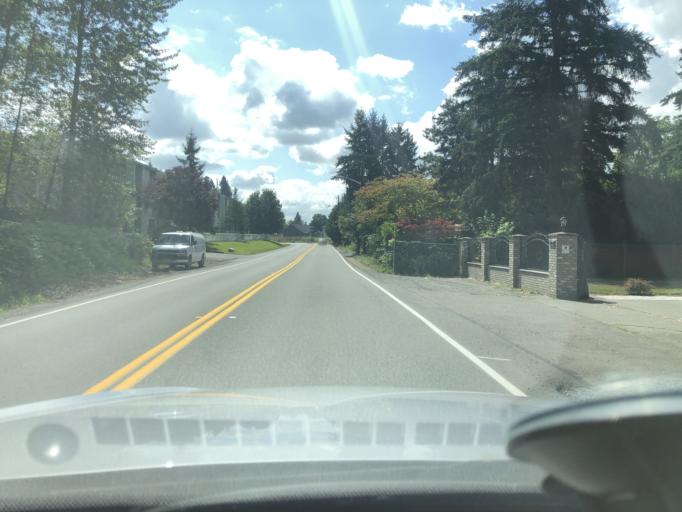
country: US
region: Washington
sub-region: King County
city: Lea Hill
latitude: 47.3189
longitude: -122.2040
